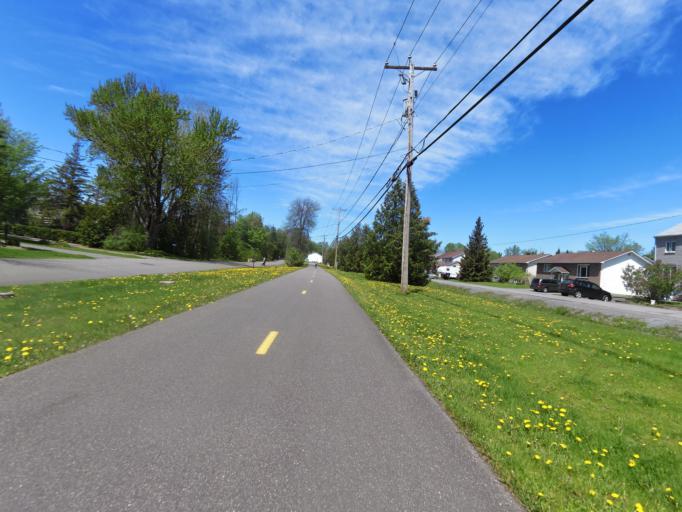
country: CA
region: Ontario
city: Bells Corners
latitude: 45.4039
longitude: -75.8708
